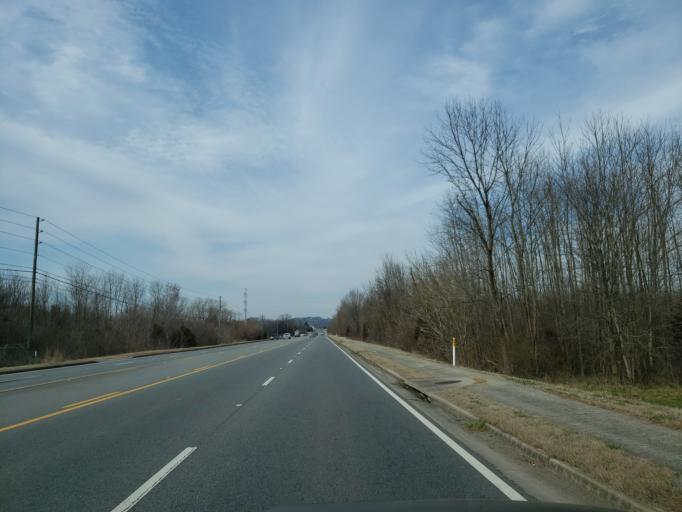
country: US
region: Georgia
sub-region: Whitfield County
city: Varnell
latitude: 34.8832
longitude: -84.9456
